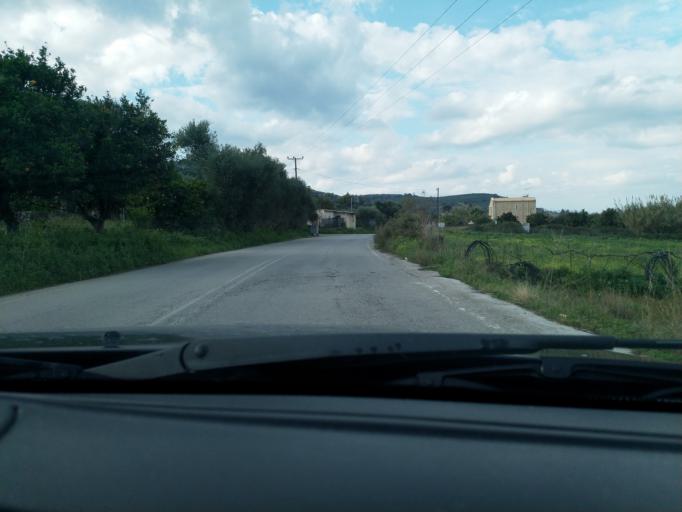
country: GR
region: Crete
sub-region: Nomos Chanias
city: Agia Marina
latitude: 35.4980
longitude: 23.9027
